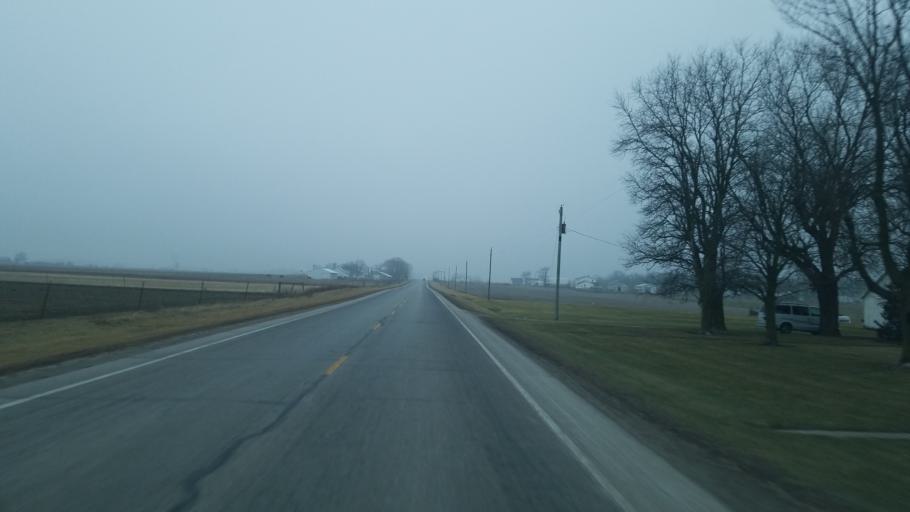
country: US
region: Indiana
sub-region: Adams County
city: Berne
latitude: 40.6593
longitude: -84.8539
